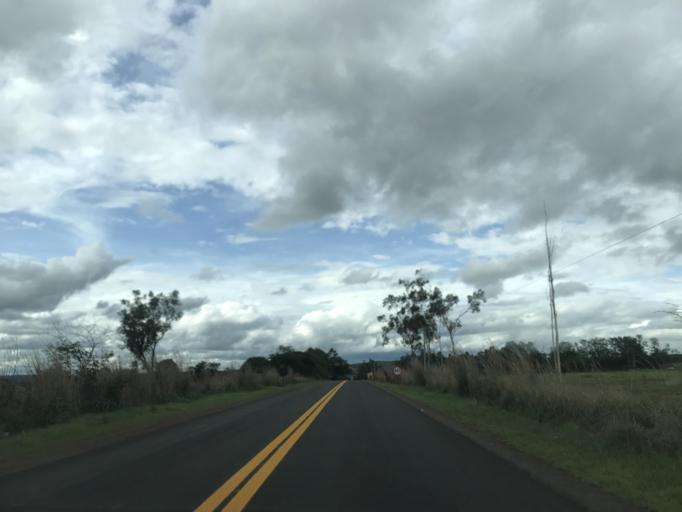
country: BR
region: Goias
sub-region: Bela Vista De Goias
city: Bela Vista de Goias
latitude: -17.0749
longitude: -48.6576
